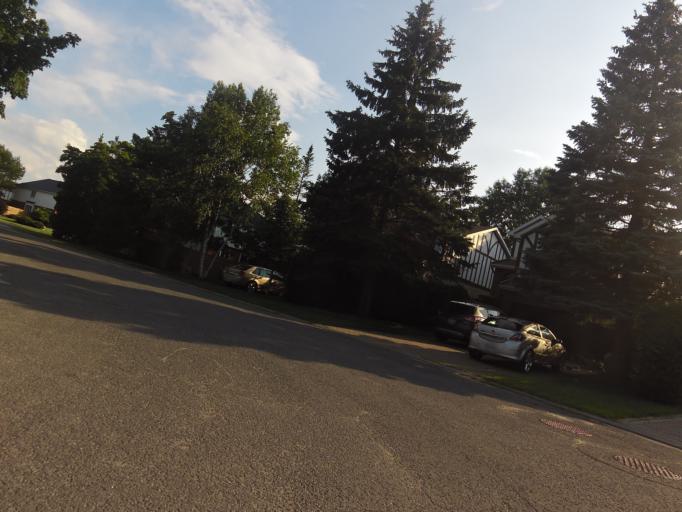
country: CA
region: Ontario
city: Bells Corners
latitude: 45.3274
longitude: -75.7759
